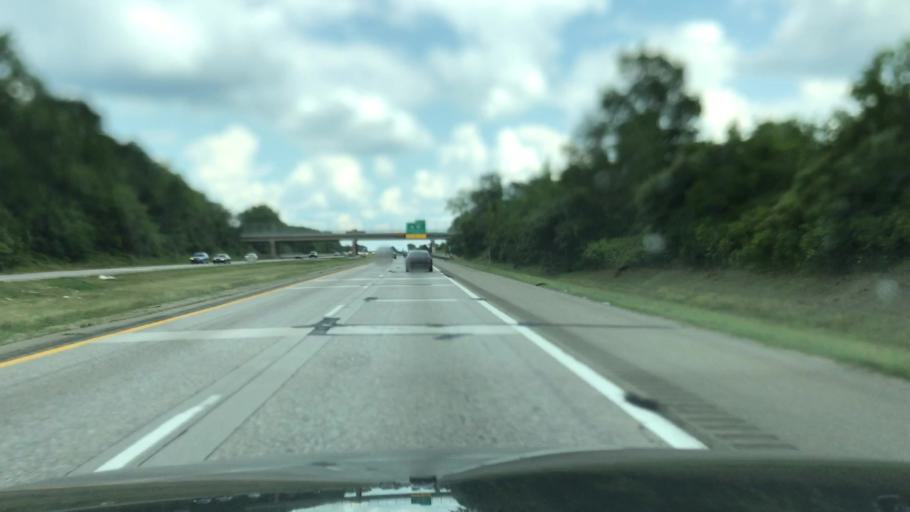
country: US
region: Michigan
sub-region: Kent County
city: East Grand Rapids
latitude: 42.9766
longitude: -85.6134
